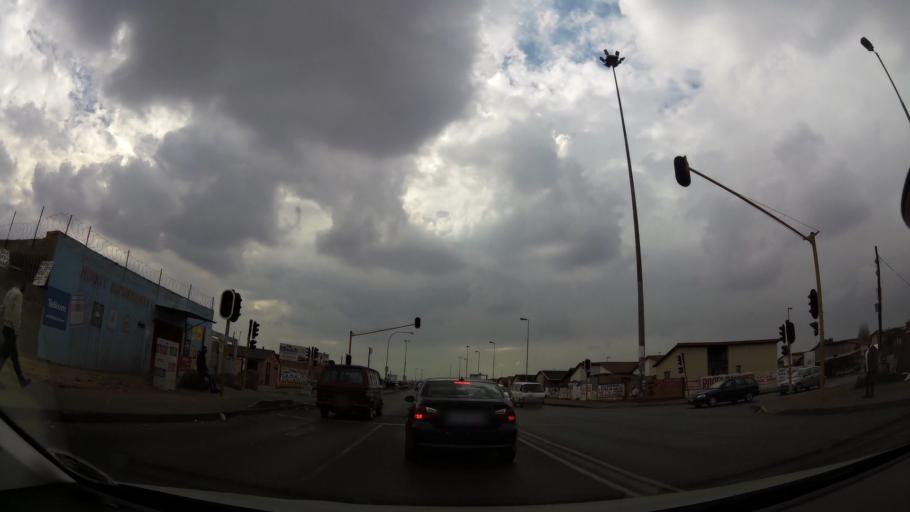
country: ZA
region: Gauteng
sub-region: City of Johannesburg Metropolitan Municipality
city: Soweto
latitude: -26.2602
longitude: 27.8563
